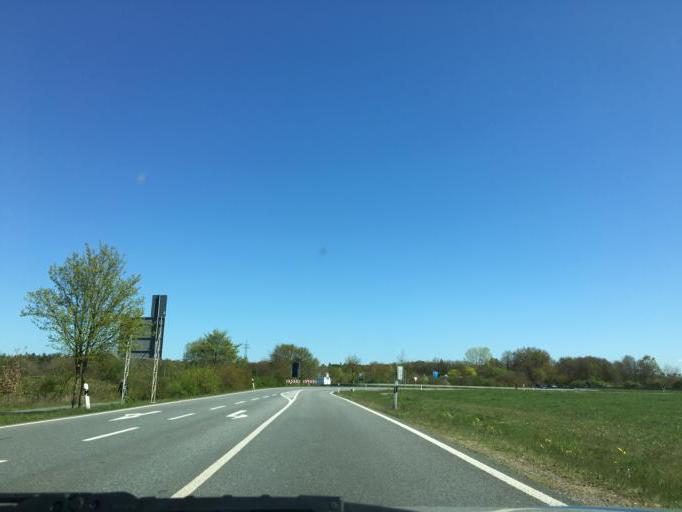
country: DE
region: Hesse
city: Obertshausen
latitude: 50.0707
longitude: 8.8727
